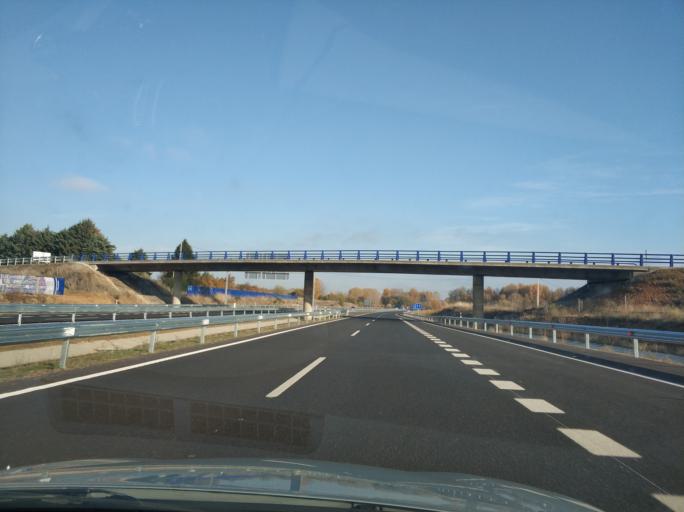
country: ES
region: Castille and Leon
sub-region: Provincia de Leon
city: Mansilla Mayor
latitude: 42.5522
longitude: -5.4563
